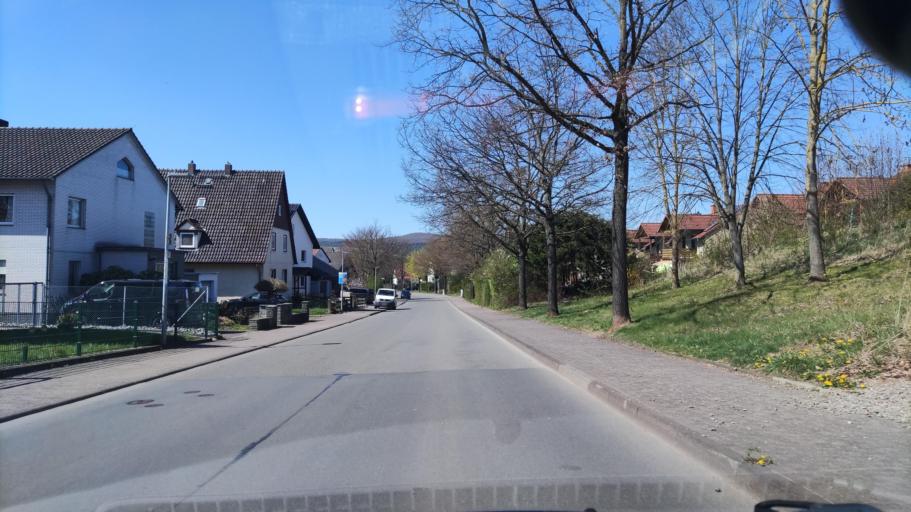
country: DE
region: Hesse
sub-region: Regierungsbezirk Kassel
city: Hofgeismar
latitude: 51.4957
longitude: 9.4004
